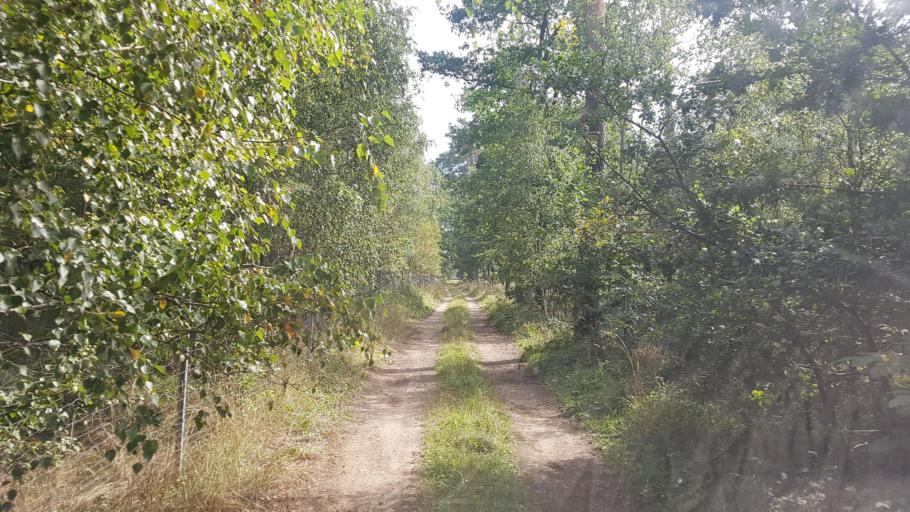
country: DE
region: Brandenburg
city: Bronkow
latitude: 51.6330
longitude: 13.8887
